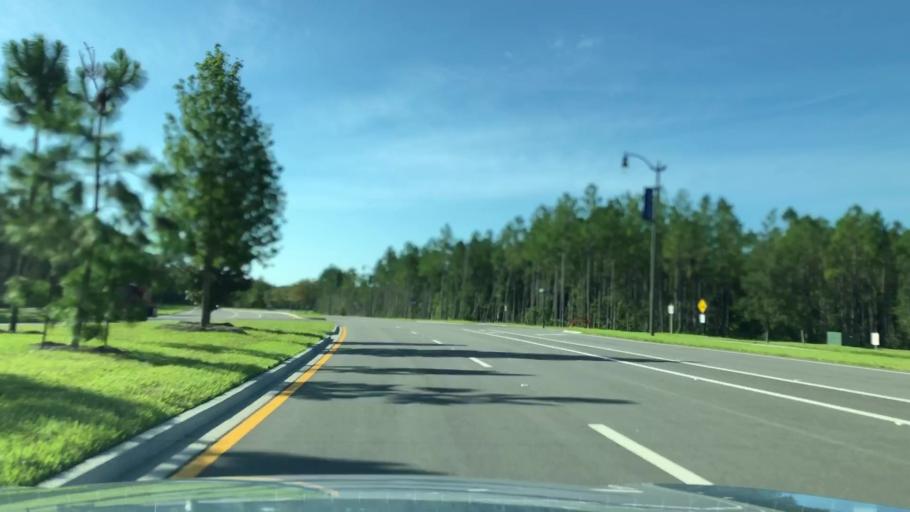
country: US
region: Florida
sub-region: Saint Johns County
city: Palm Valley
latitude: 30.0843
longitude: -81.4052
